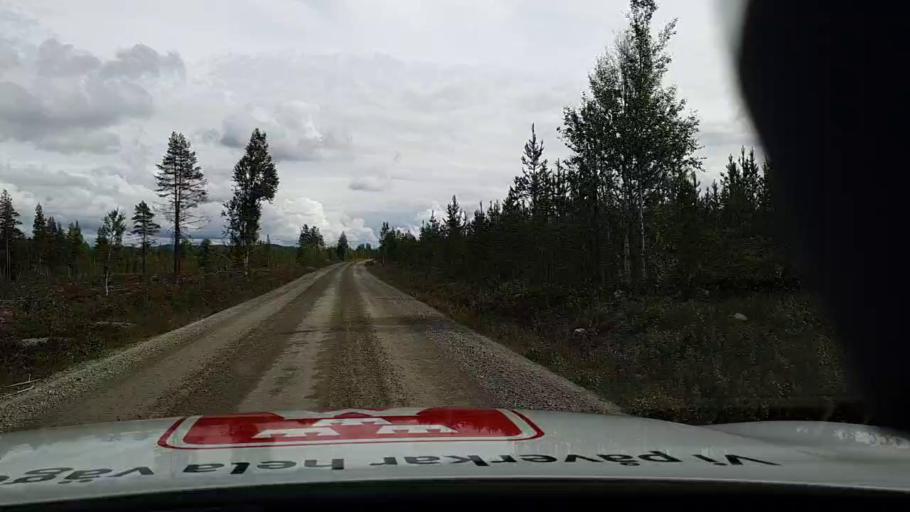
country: SE
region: Jaemtland
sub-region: Are Kommun
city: Jarpen
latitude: 62.5082
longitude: 13.4949
